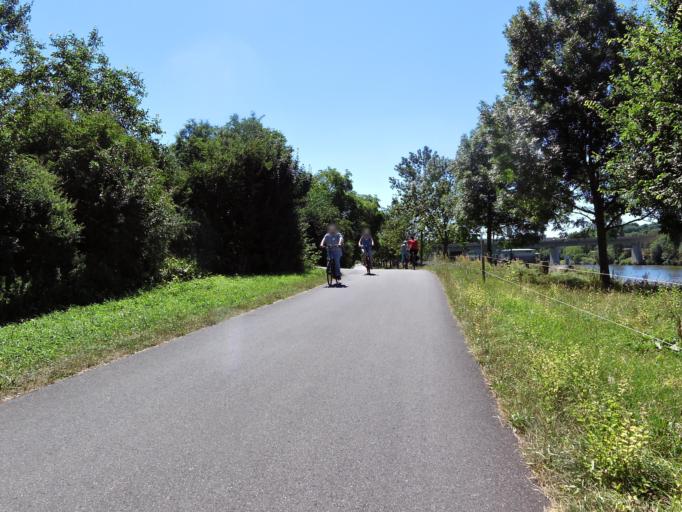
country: DE
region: Bavaria
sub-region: Regierungsbezirk Unterfranken
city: Sommerhausen
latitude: 49.6810
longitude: 10.0357
